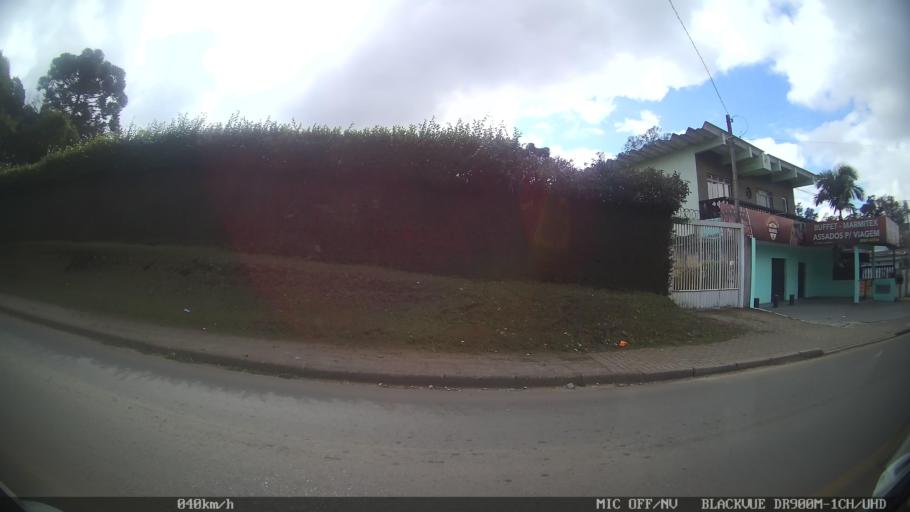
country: BR
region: Parana
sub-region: Colombo
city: Colombo
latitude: -25.3481
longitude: -49.2020
